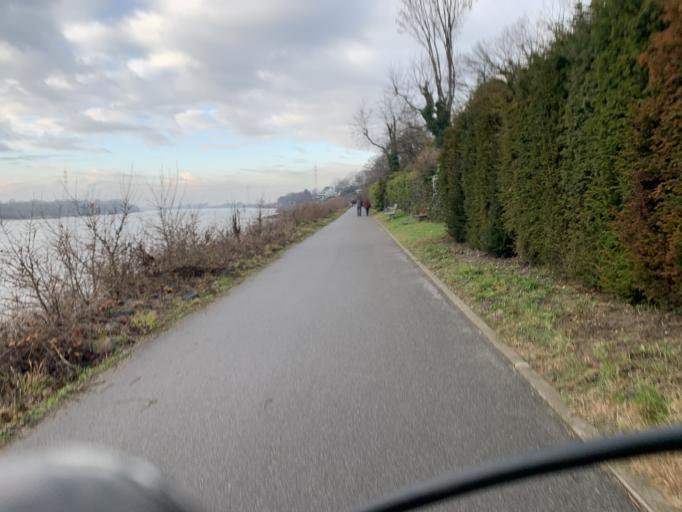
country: DE
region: North Rhine-Westphalia
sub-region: Regierungsbezirk Dusseldorf
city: Meerbusch
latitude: 51.3277
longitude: 6.7289
